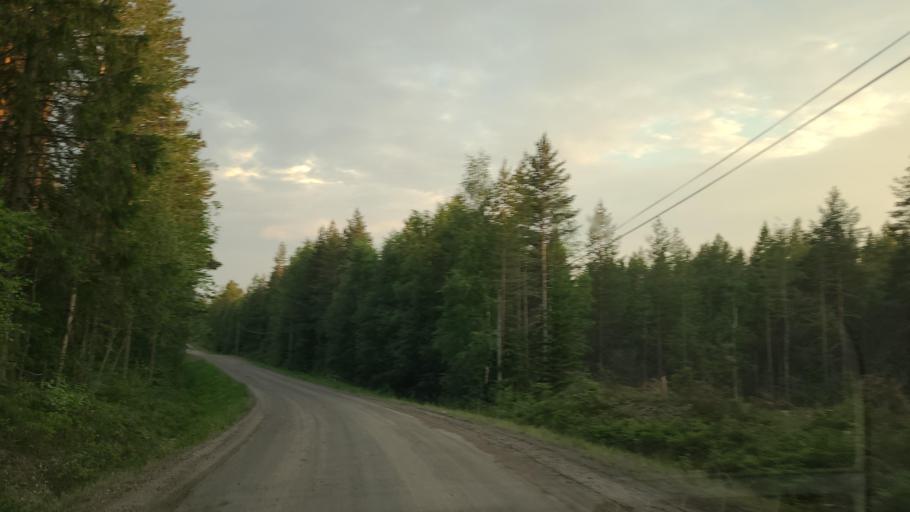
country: SE
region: Vaesterbotten
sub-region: Robertsfors Kommun
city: Robertsfors
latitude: 64.0769
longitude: 20.8871
